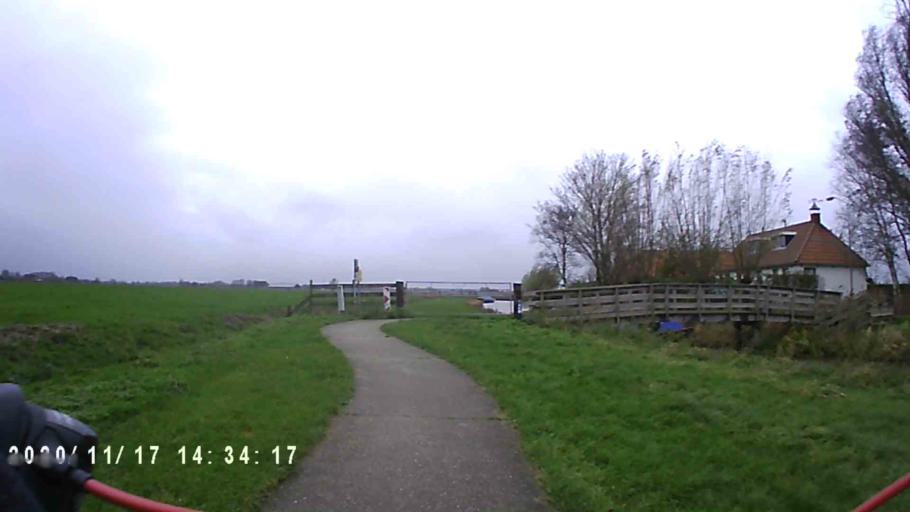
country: NL
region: Groningen
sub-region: Gemeente Zuidhorn
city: Oldehove
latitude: 53.2881
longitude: 6.3651
